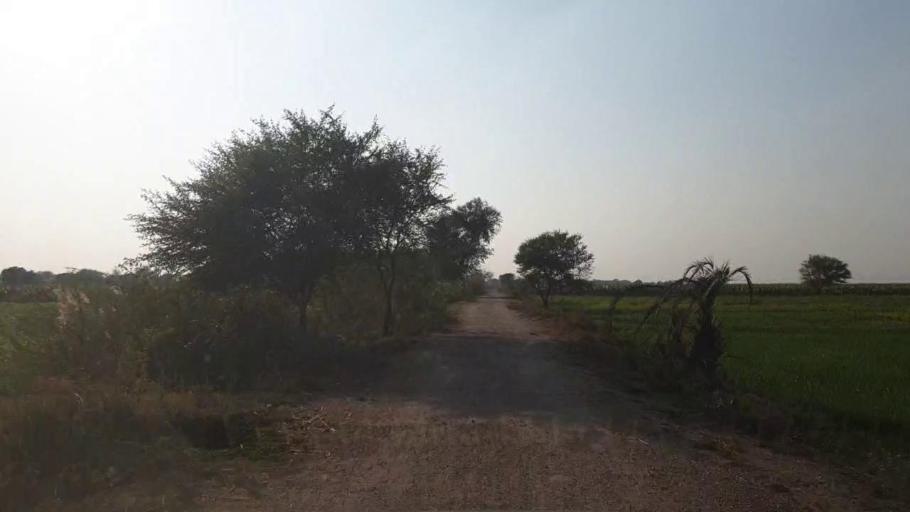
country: PK
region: Sindh
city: Mirpur Khas
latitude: 25.4172
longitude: 68.9472
